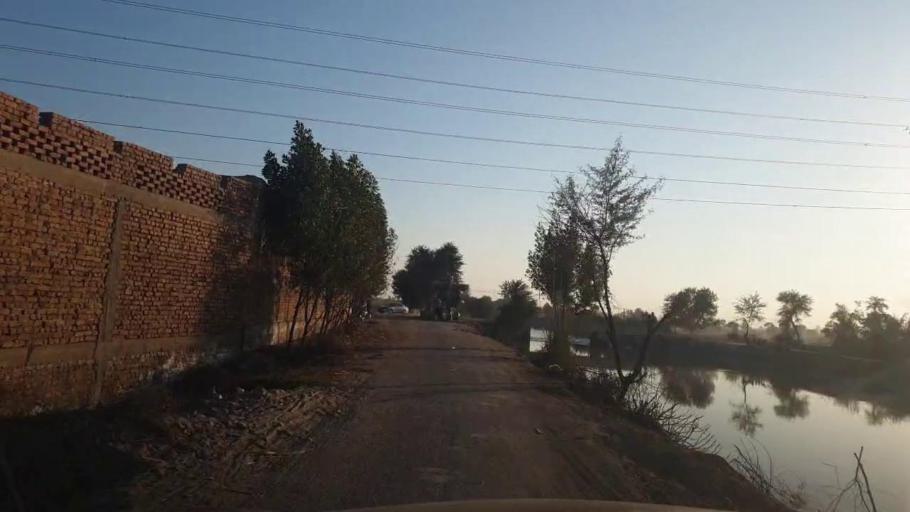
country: PK
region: Sindh
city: Mirpur Mathelo
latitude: 27.9892
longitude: 69.4647
